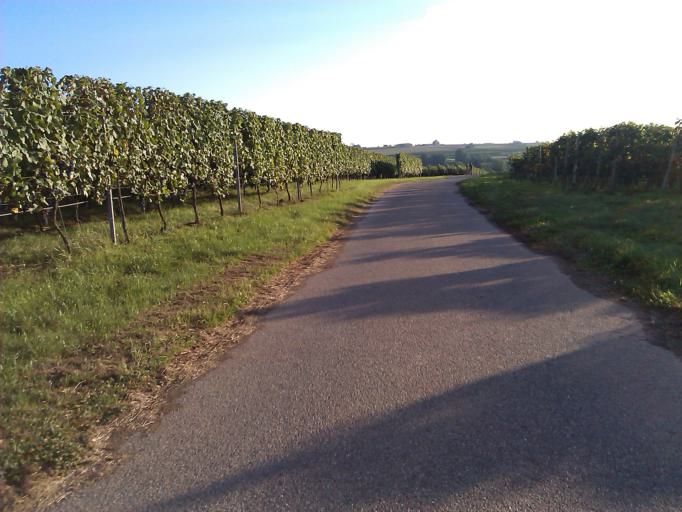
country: DE
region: Baden-Wuerttemberg
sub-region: Regierungsbezirk Stuttgart
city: Lauffen am Neckar
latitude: 49.0982
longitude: 9.1607
